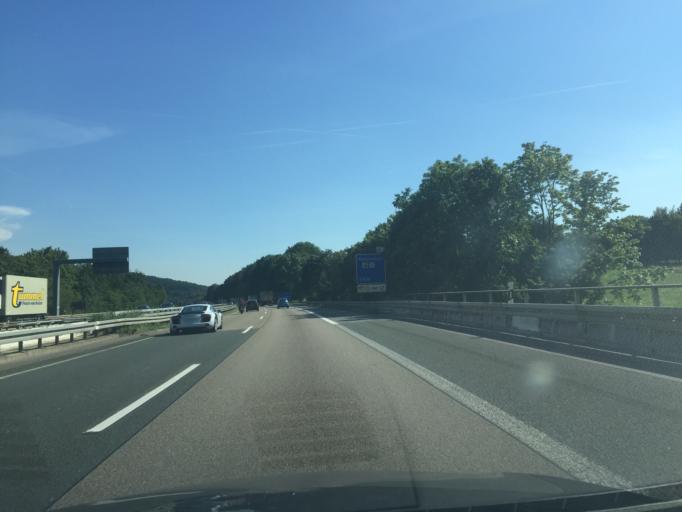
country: DE
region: Hesse
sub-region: Regierungsbezirk Giessen
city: Sinn
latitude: 50.6532
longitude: 8.3206
